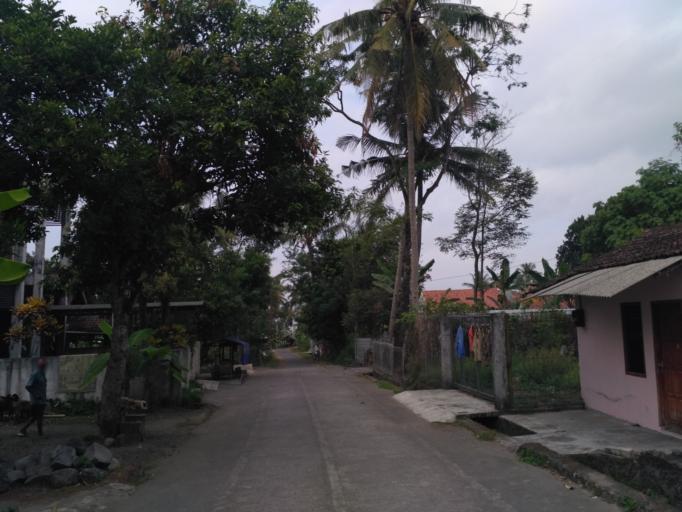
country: ID
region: Daerah Istimewa Yogyakarta
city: Melati
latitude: -7.7054
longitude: 110.4081
